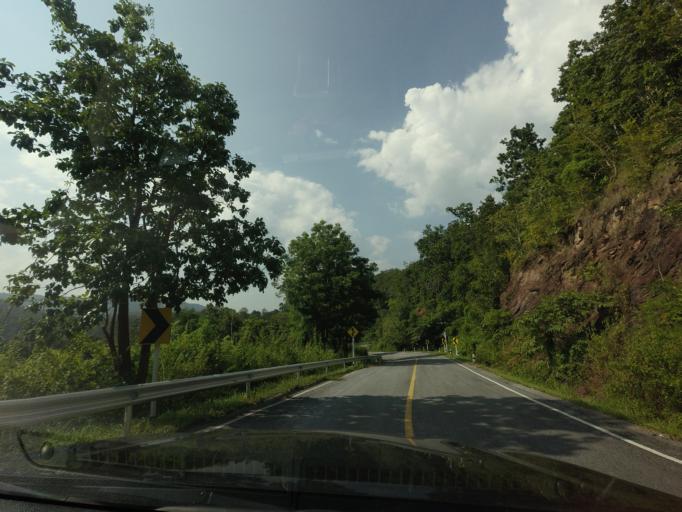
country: TH
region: Uttaradit
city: Ban Khok
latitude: 18.2498
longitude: 100.9971
